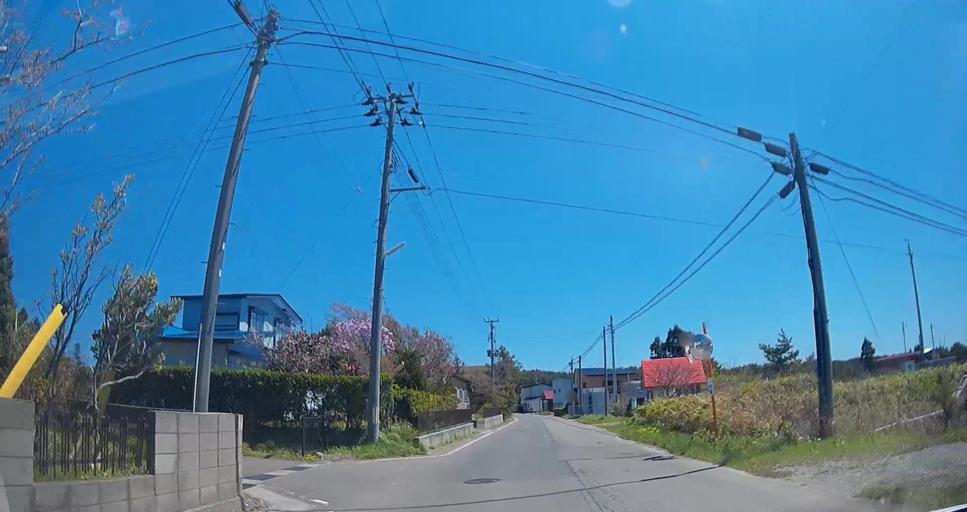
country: JP
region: Aomori
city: Mutsu
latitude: 41.2358
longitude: 141.3972
